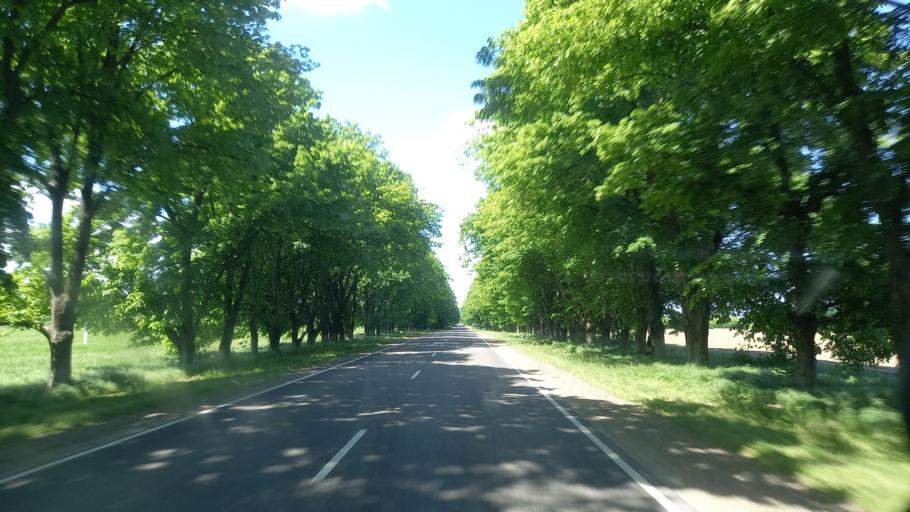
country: RU
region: Krasnodarskiy
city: Kazanskaya
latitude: 45.3768
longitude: 40.4731
